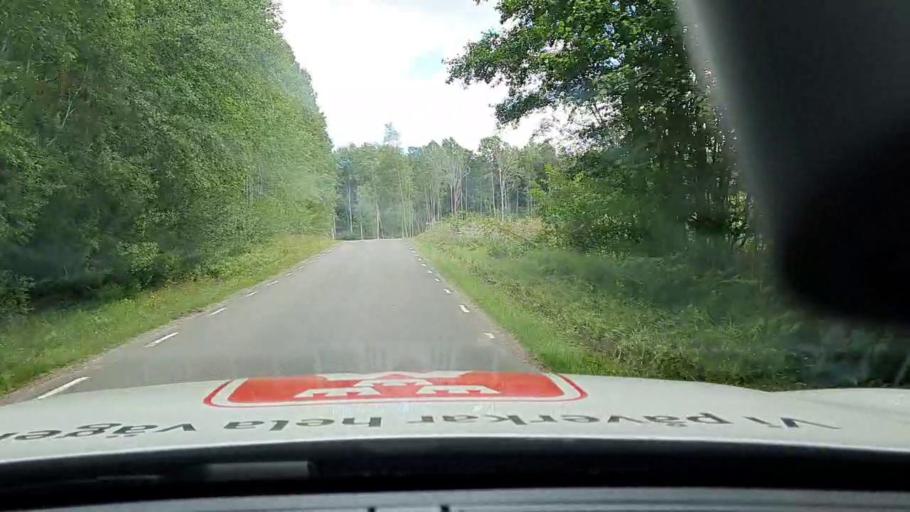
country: SE
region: Vaestra Goetaland
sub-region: Karlsborgs Kommun
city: Molltorp
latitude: 58.5724
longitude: 14.2565
